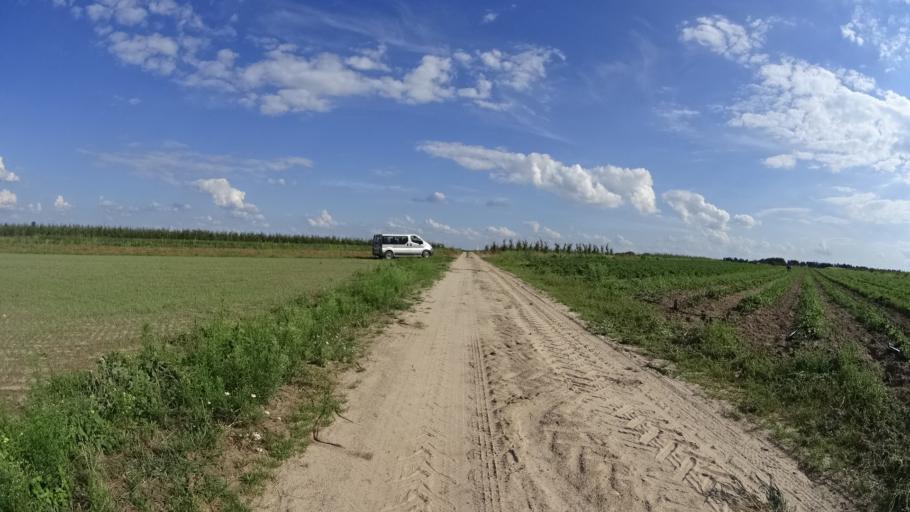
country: PL
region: Masovian Voivodeship
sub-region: Powiat bialobrzeski
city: Wysmierzyce
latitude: 51.6622
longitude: 20.8178
